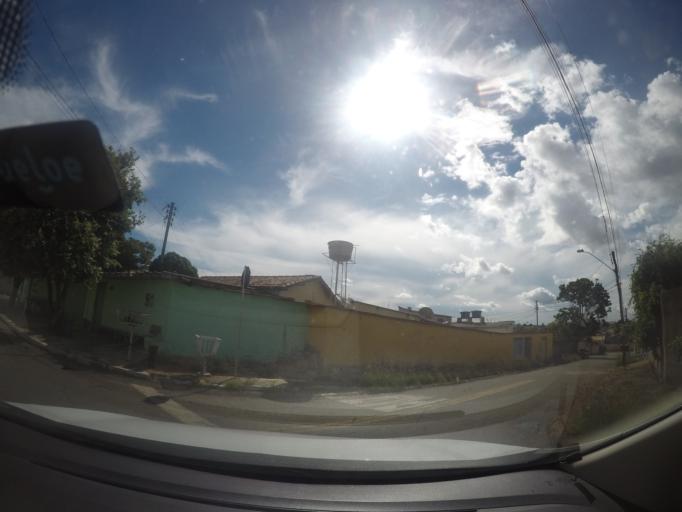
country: BR
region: Goias
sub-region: Goiania
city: Goiania
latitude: -16.6799
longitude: -49.3018
